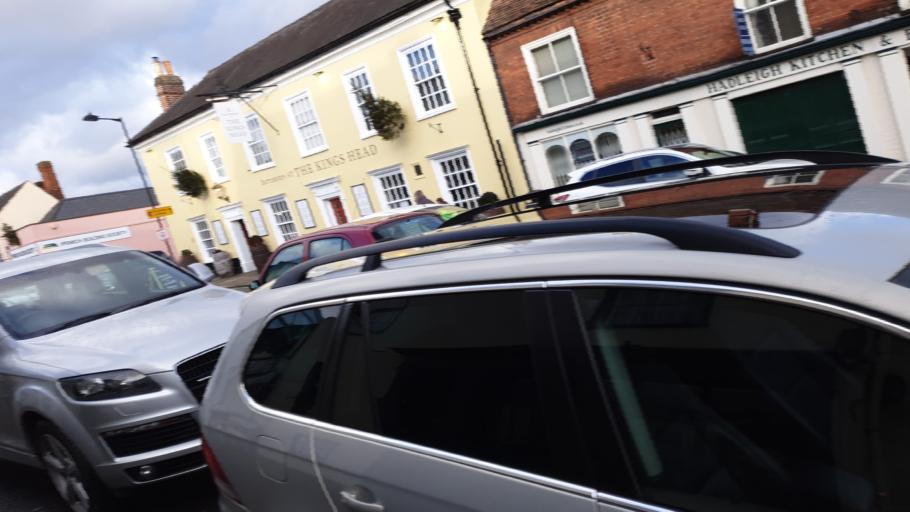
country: GB
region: England
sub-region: Suffolk
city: Hadleigh
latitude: 52.0447
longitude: 0.9531
